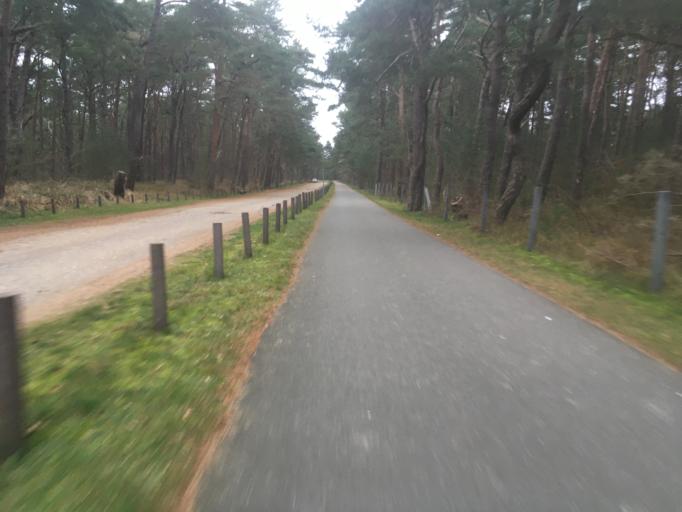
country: DE
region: Mecklenburg-Vorpommern
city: Sagard
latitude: 54.4681
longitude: 13.5672
